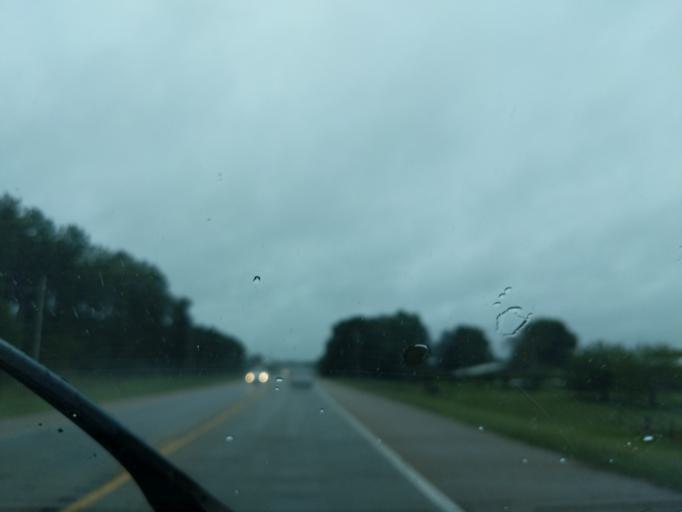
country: US
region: Louisiana
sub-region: Webster Parish
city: Minden
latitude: 32.5893
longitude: -93.2478
